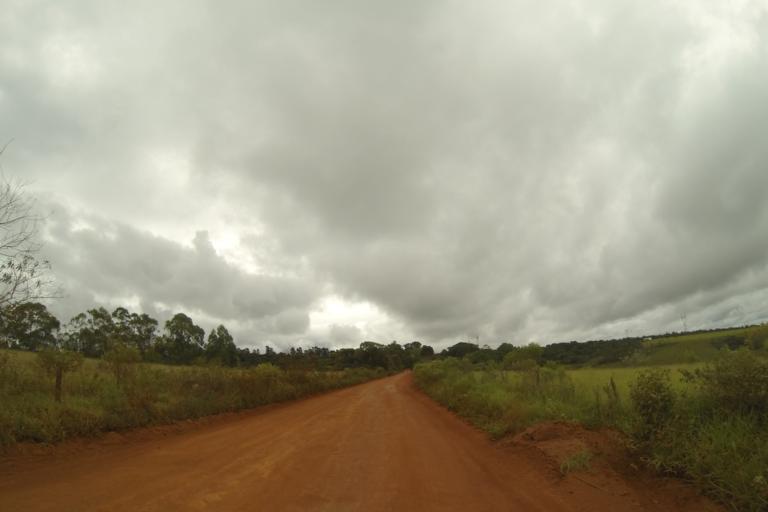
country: BR
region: Minas Gerais
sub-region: Campos Altos
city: Campos Altos
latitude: -19.8723
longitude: -46.3044
